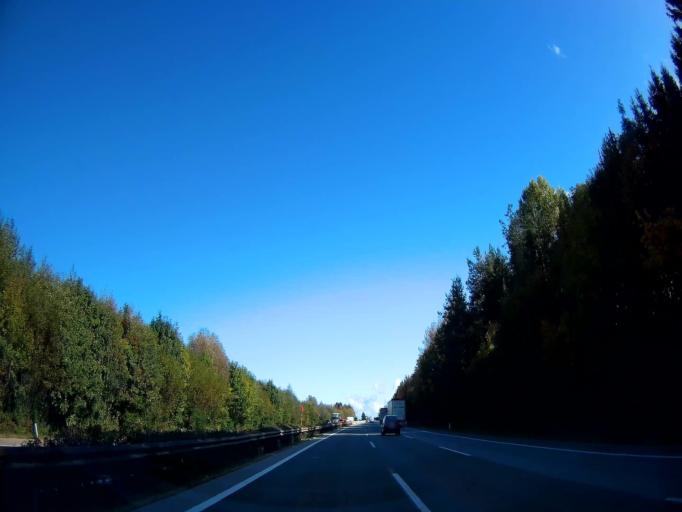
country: AT
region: Carinthia
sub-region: Politischer Bezirk Villach Land
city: Wernberg
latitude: 46.6234
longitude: 13.9299
